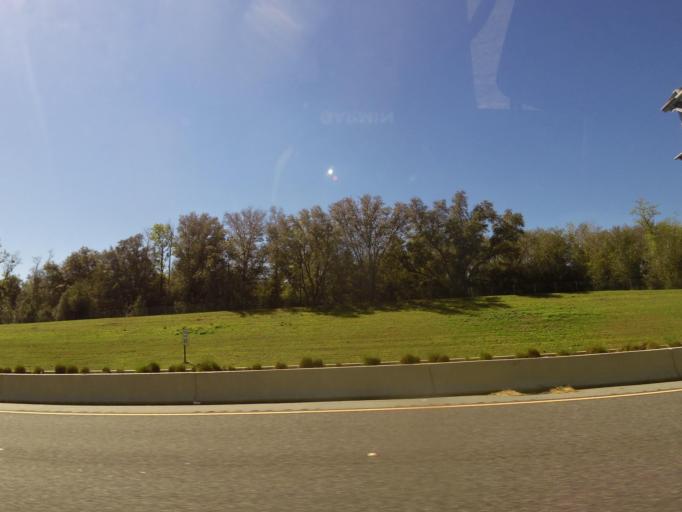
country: US
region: Florida
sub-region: Lake County
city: Mount Plymouth
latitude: 28.7958
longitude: -81.5816
